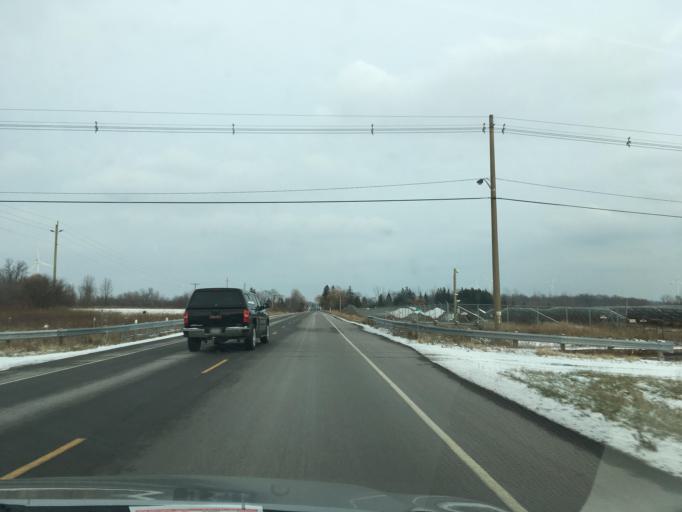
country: CA
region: Ontario
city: Norfolk County
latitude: 42.8162
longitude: -80.0397
